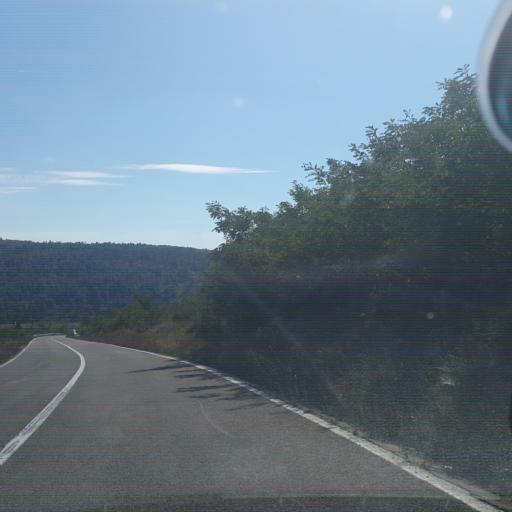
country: RS
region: Central Serbia
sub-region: Zajecarski Okrug
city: Knjazevac
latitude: 43.4740
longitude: 22.2274
